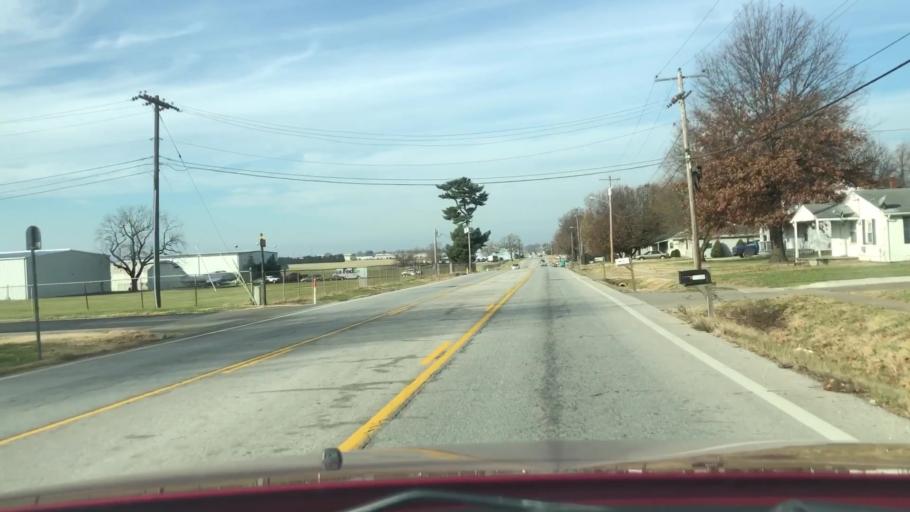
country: US
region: Missouri
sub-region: Greene County
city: Springfield
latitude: 37.2249
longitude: -93.2419
